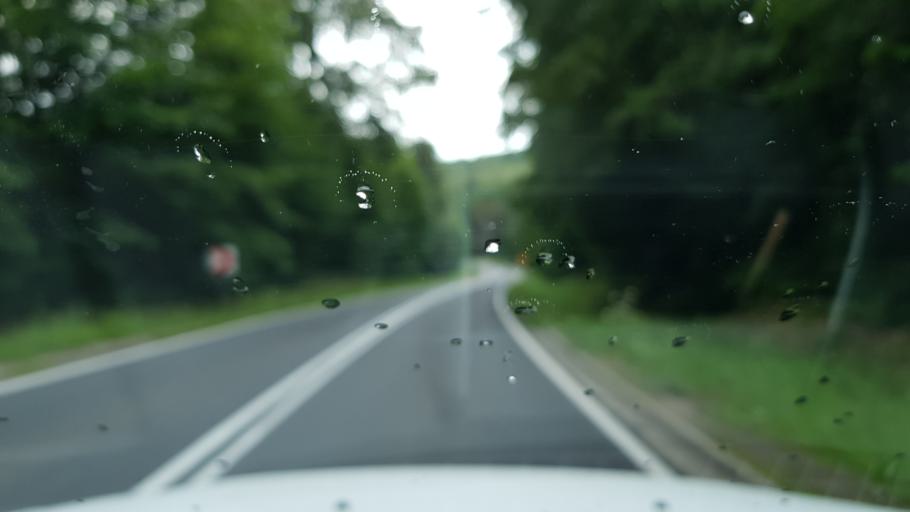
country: PL
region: West Pomeranian Voivodeship
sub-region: Powiat koszalinski
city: Bobolice
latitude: 53.9381
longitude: 16.6280
